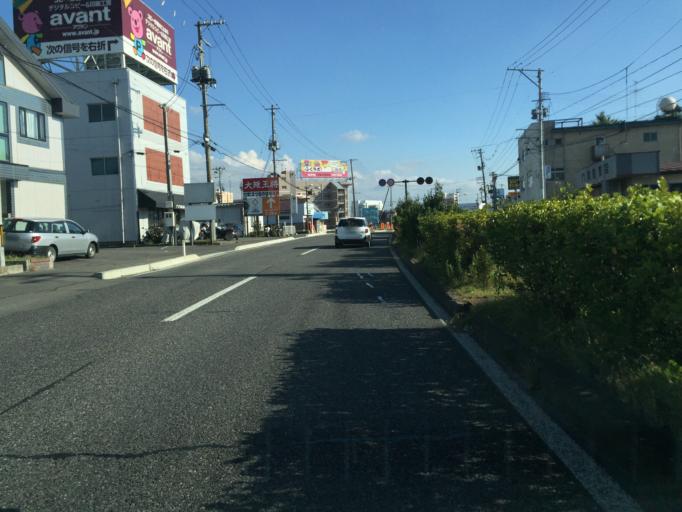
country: JP
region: Fukushima
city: Koriyama
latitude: 37.4105
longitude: 140.3492
